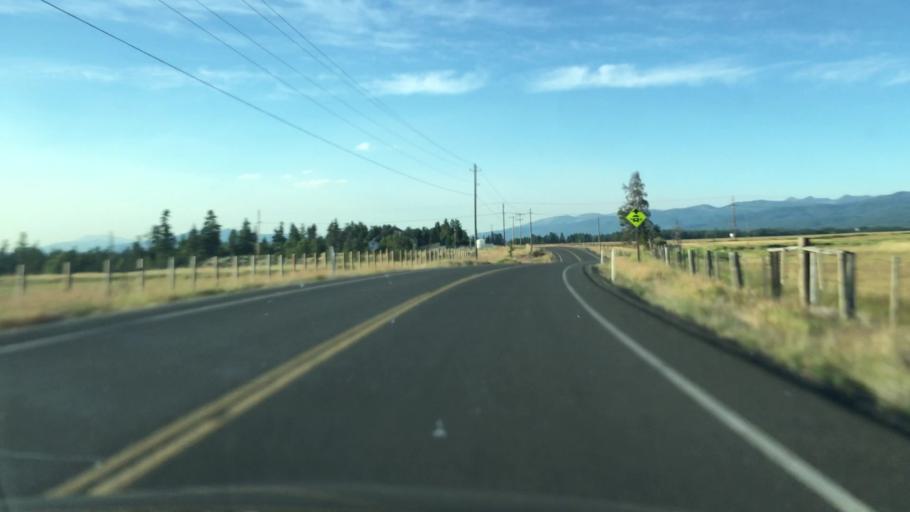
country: US
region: Idaho
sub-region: Valley County
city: McCall
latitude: 44.7717
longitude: -116.0781
